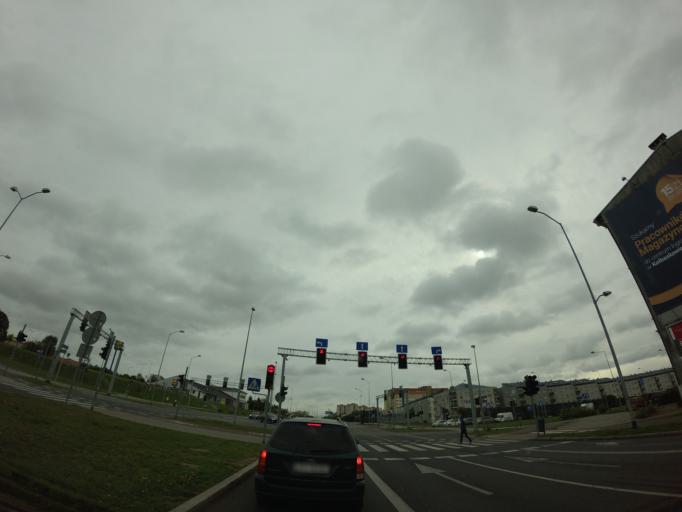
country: PL
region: West Pomeranian Voivodeship
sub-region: Szczecin
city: Szczecin
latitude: 53.4549
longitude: 14.5431
